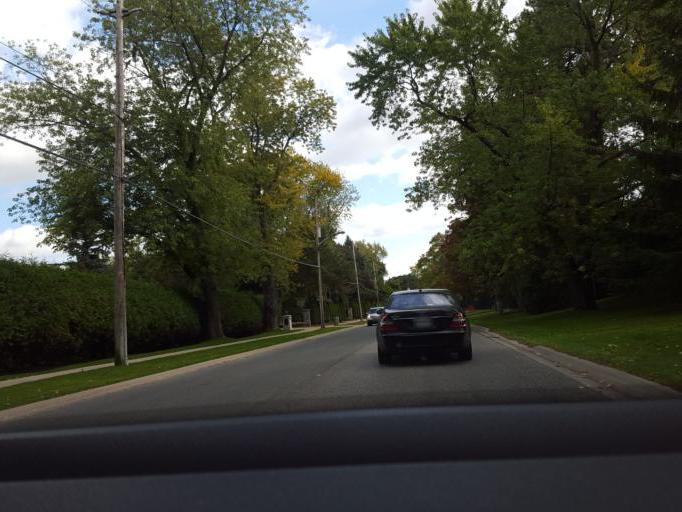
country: CA
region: Ontario
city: Willowdale
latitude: 43.7360
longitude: -79.3696
